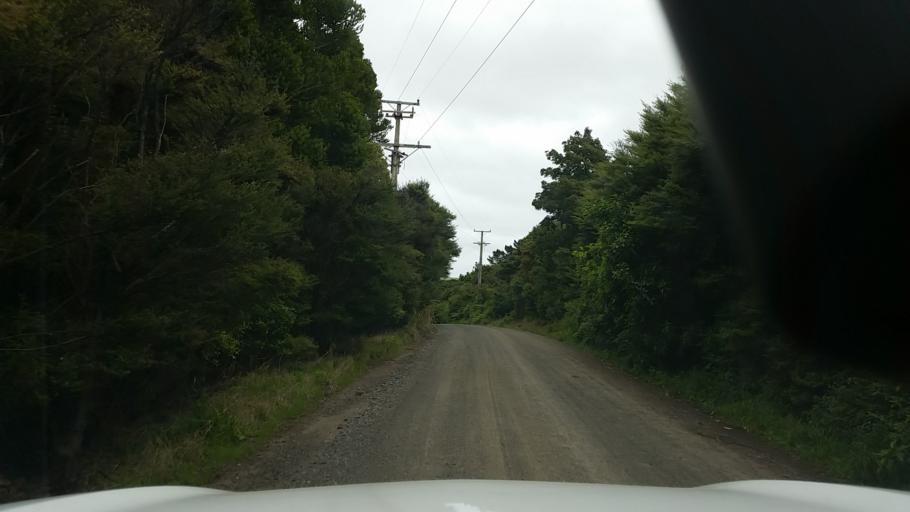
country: NZ
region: Auckland
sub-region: Auckland
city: Muriwai Beach
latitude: -36.8754
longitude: 174.4810
